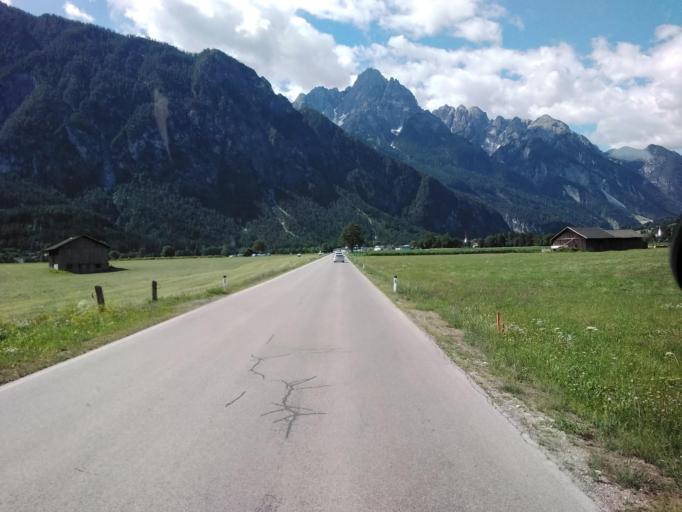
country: AT
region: Tyrol
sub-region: Politischer Bezirk Lienz
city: Lienz
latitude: 46.8227
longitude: 12.7680
